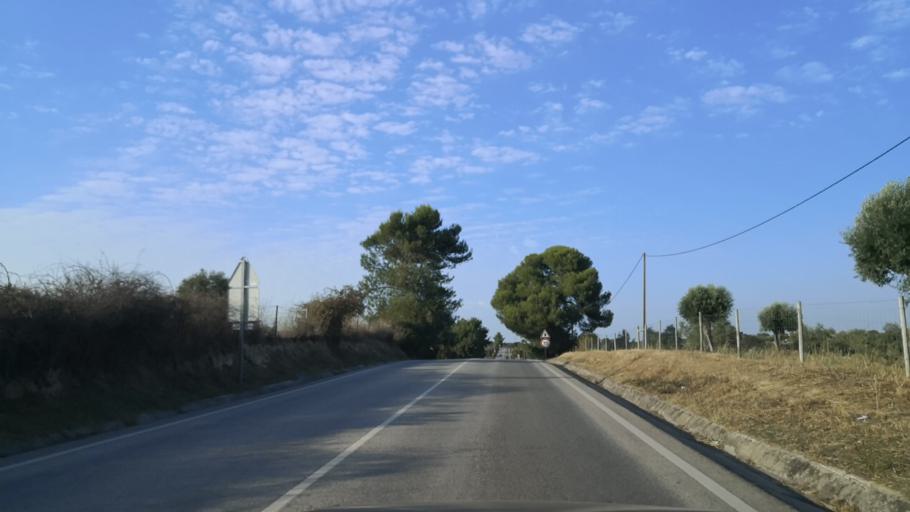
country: PT
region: Santarem
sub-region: Alcanena
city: Alcanena
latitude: 39.3878
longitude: -8.6505
